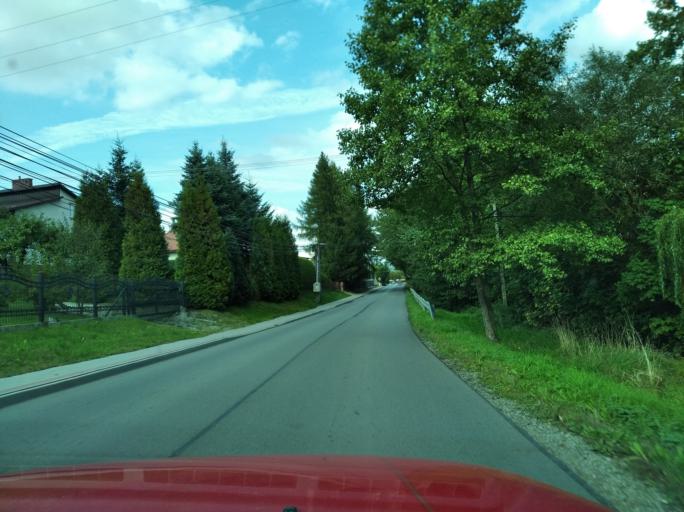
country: PL
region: Subcarpathian Voivodeship
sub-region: Powiat rzeszowski
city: Tyczyn
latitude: 49.9508
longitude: 22.0265
